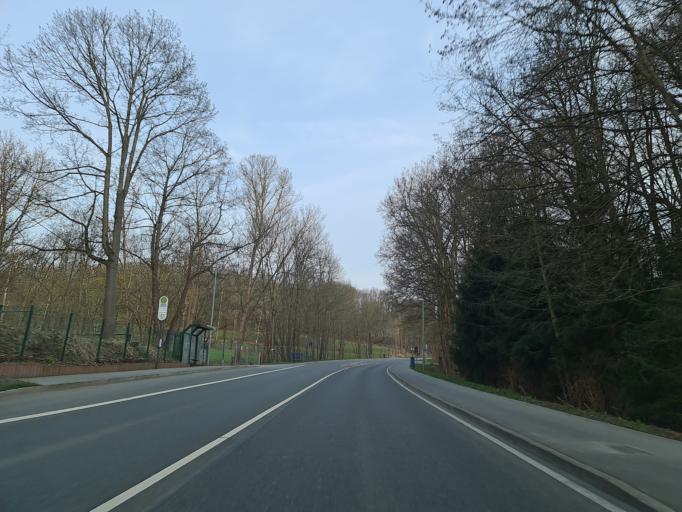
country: DE
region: Saxony
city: Plauen
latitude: 50.4712
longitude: 12.1474
